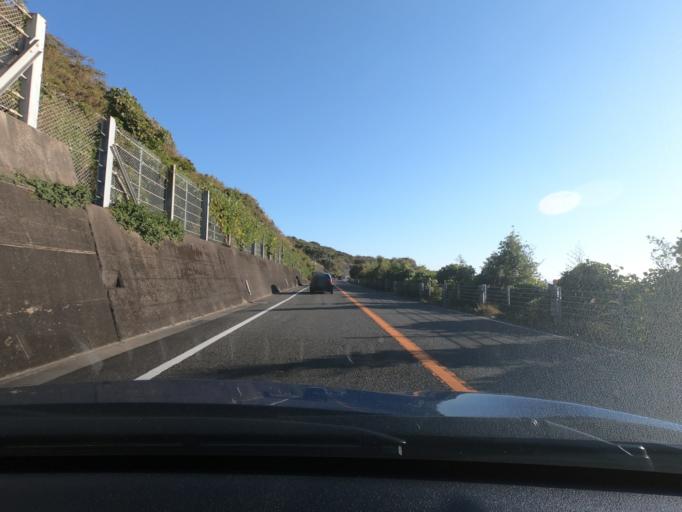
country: JP
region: Kagoshima
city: Akune
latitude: 31.9557
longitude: 130.2157
